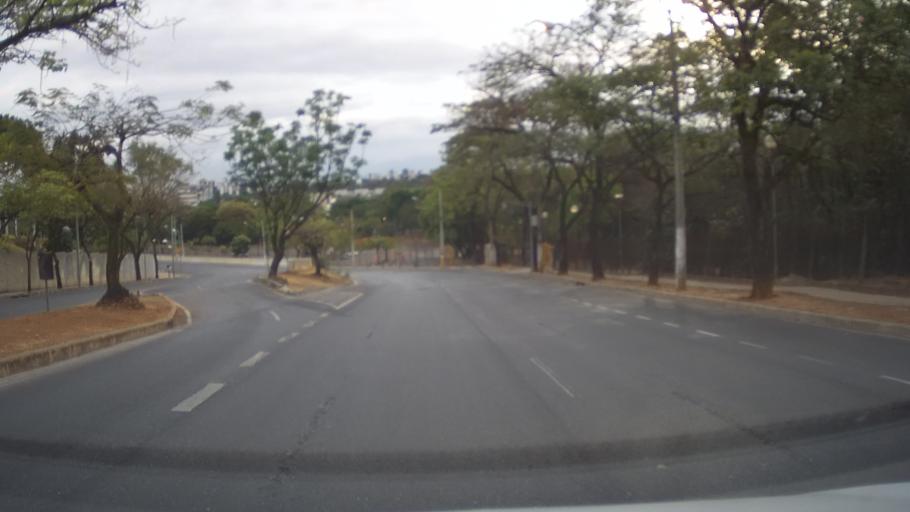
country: BR
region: Minas Gerais
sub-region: Belo Horizonte
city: Belo Horizonte
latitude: -19.8694
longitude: -43.9711
